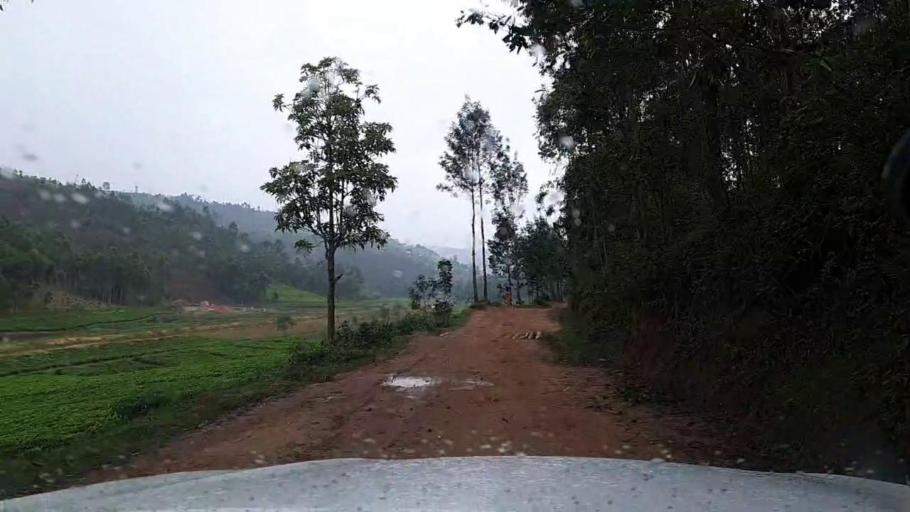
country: RW
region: Northern Province
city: Byumba
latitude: -1.6514
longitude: 29.9323
